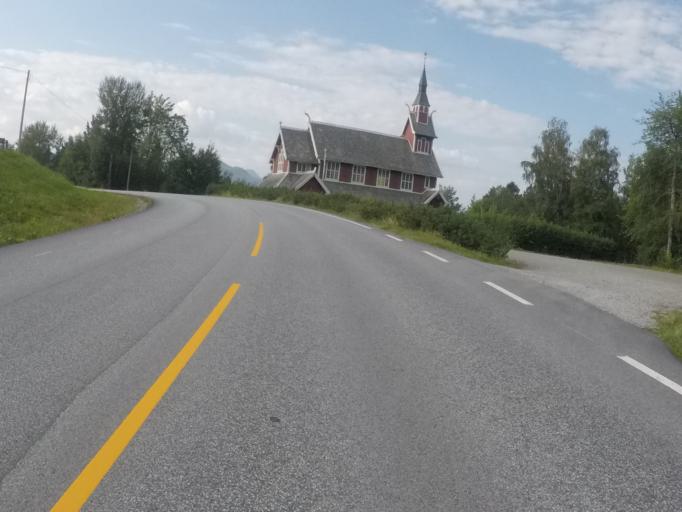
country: NO
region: More og Romsdal
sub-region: Molde
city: Hjelset
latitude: 62.6863
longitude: 7.4550
